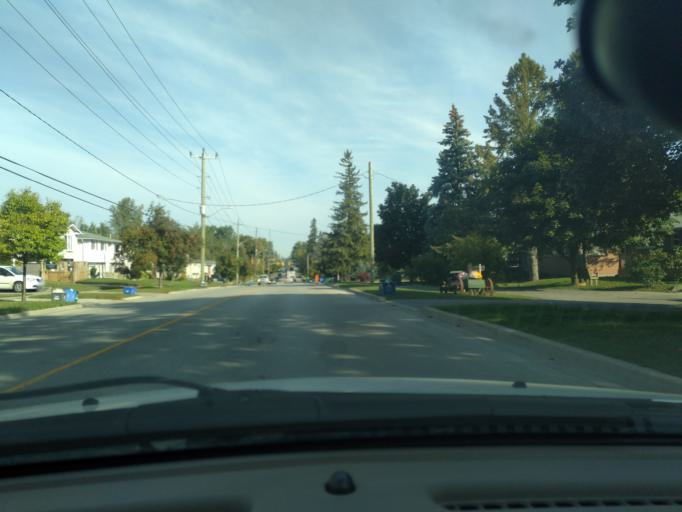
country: CA
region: Ontario
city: Barrie
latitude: 44.3631
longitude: -79.6681
